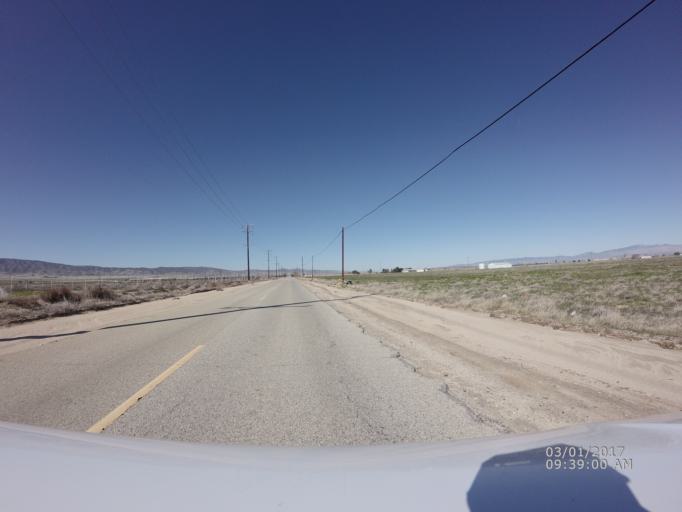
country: US
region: California
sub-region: Los Angeles County
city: Leona Valley
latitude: 34.6894
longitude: -118.2779
